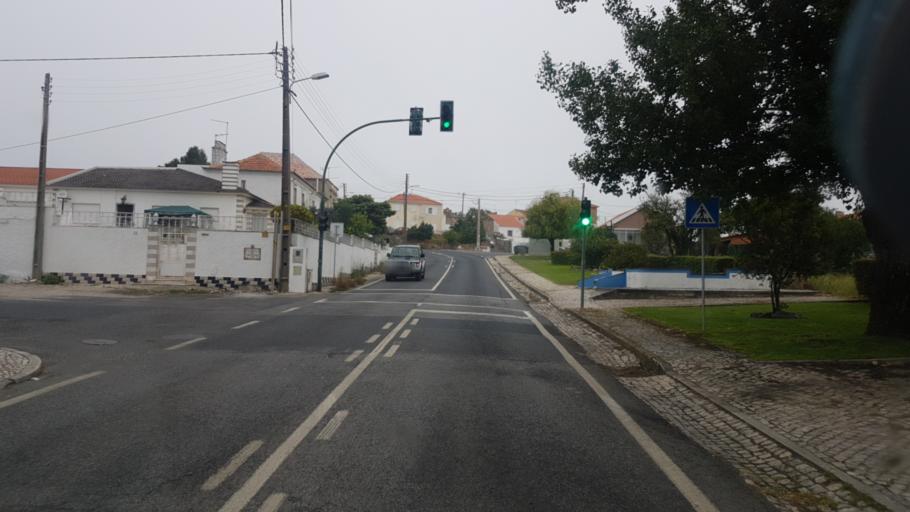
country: PT
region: Lisbon
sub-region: Sintra
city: Sintra
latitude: 38.8313
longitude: -9.3703
